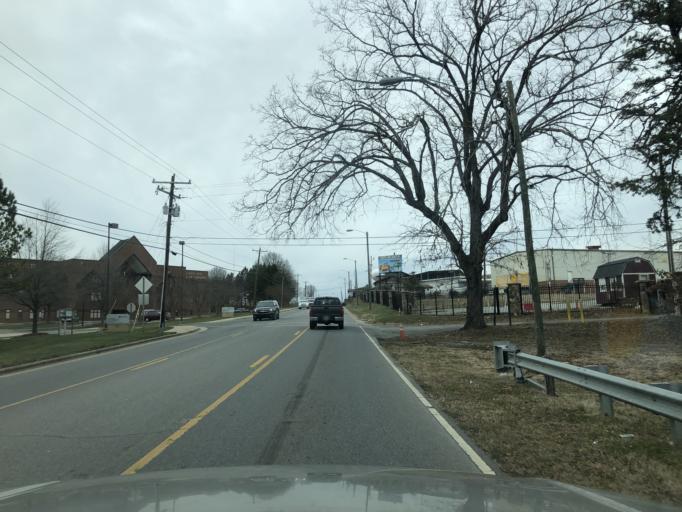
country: US
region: North Carolina
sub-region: Cleveland County
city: Shelby
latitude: 35.2785
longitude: -81.4886
